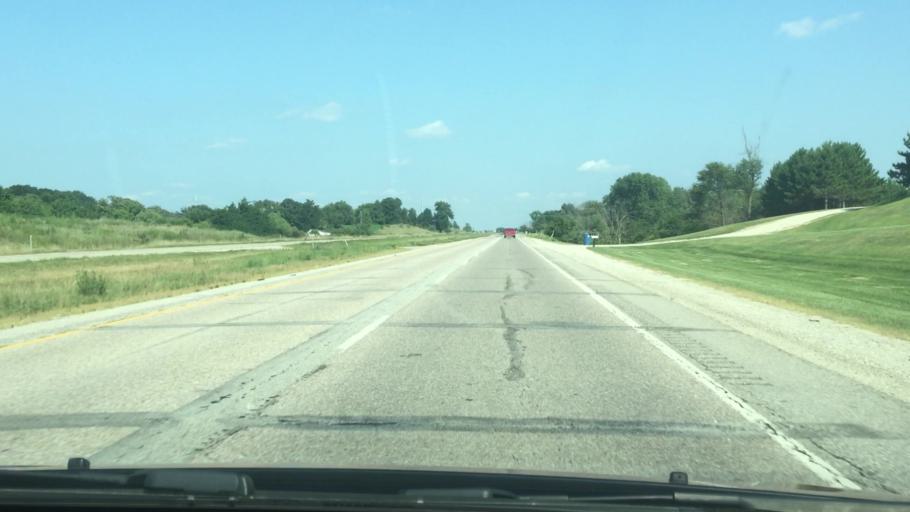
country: US
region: Iowa
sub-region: Scott County
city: Blue Grass
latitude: 41.5151
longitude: -90.8234
